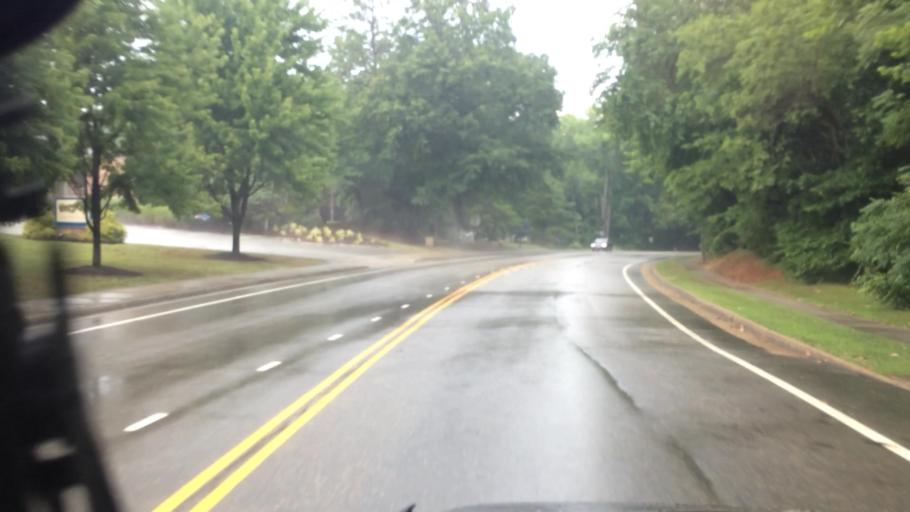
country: US
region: Virginia
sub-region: City of Williamsburg
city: Williamsburg
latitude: 37.2762
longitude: -76.7062
